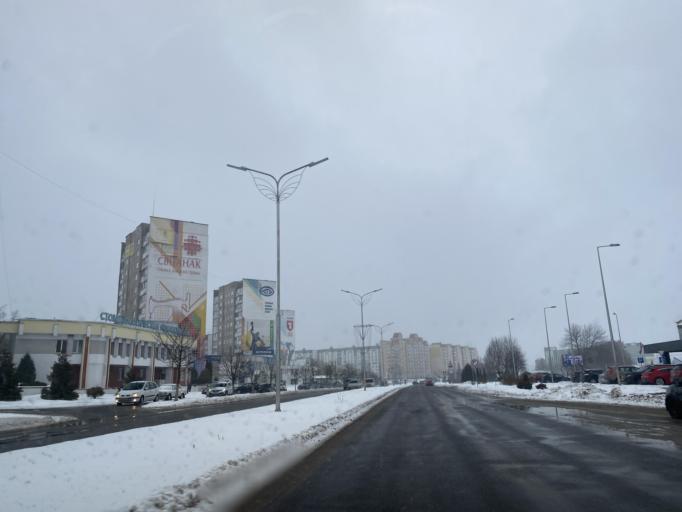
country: BY
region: Minsk
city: Horad Zhodzina
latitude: 54.0955
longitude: 28.3046
